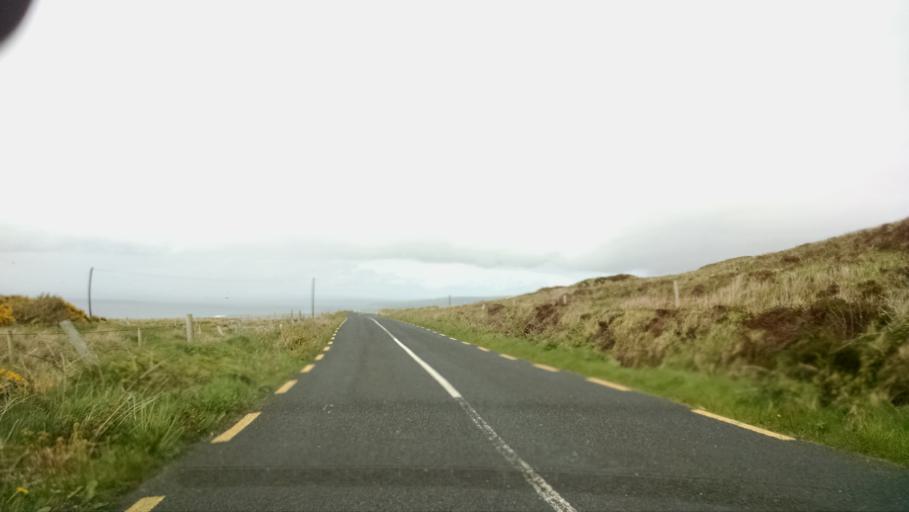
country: IE
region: Munster
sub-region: An Clar
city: Kilrush
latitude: 52.9820
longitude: -9.4189
